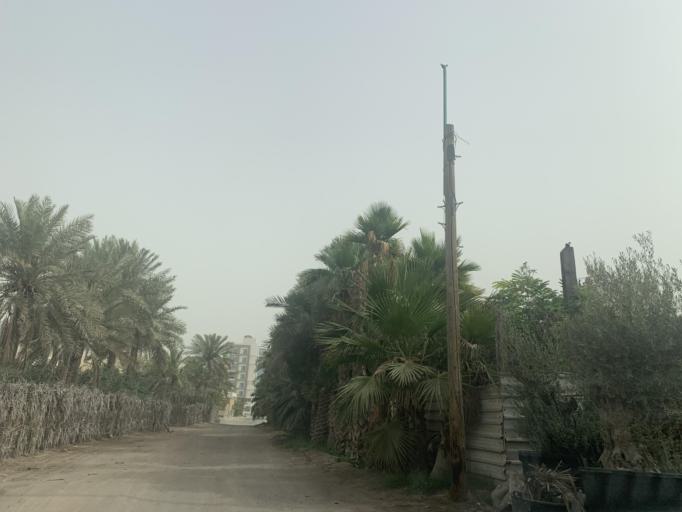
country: BH
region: Manama
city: Jidd Hafs
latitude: 26.2230
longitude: 50.5554
